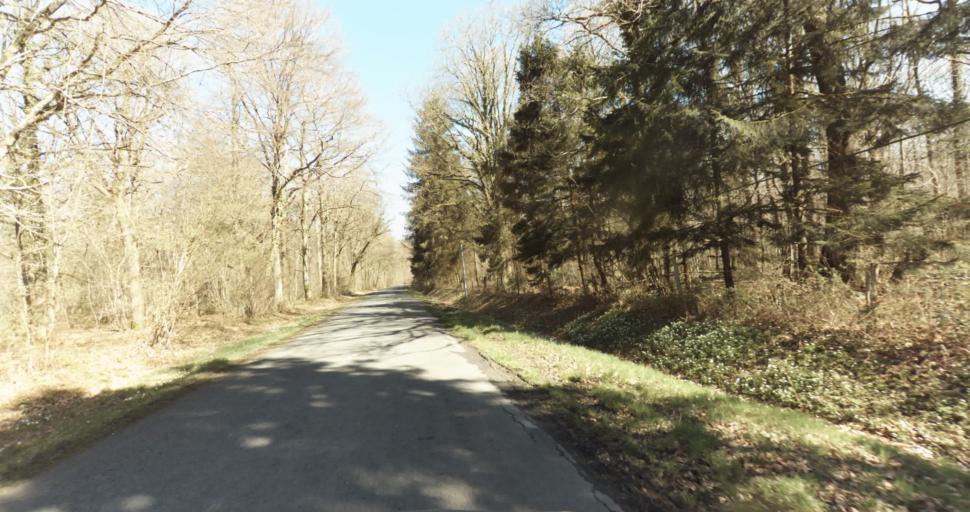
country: FR
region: Lower Normandy
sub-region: Departement de l'Orne
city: Trun
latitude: 48.9301
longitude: 0.0693
